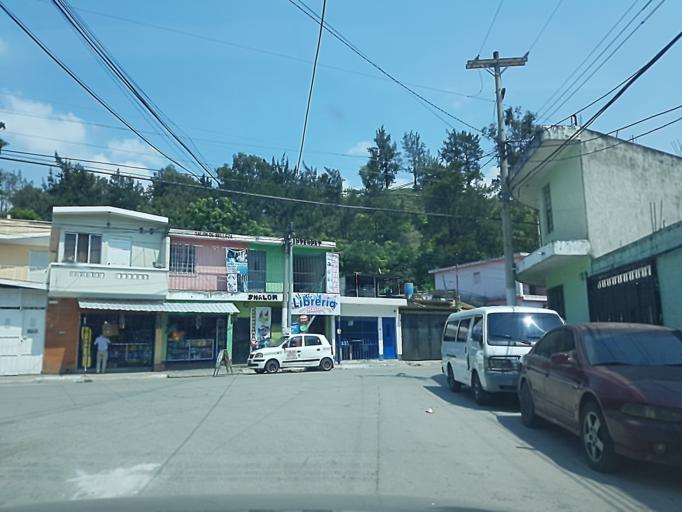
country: GT
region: Guatemala
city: Petapa
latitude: 14.5238
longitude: -90.5492
